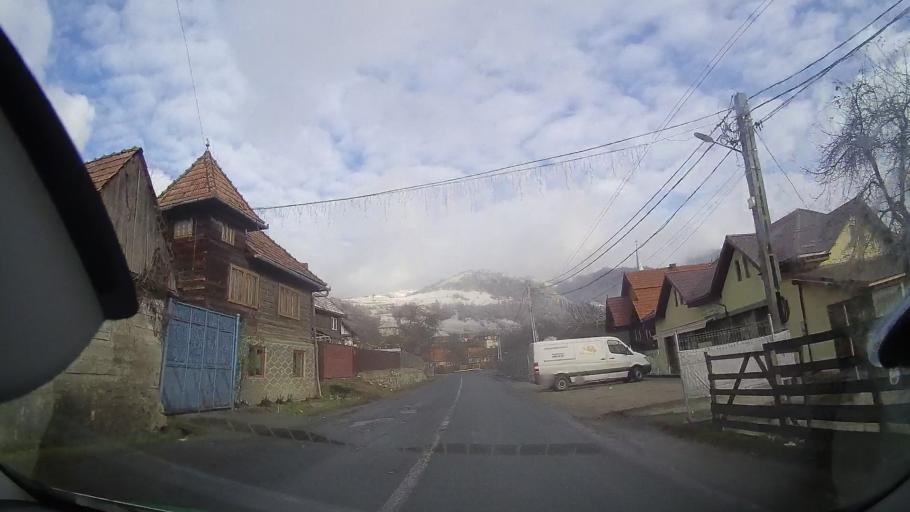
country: RO
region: Alba
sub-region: Comuna Lupsa
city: Lupsa
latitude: 46.3798
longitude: 23.2252
